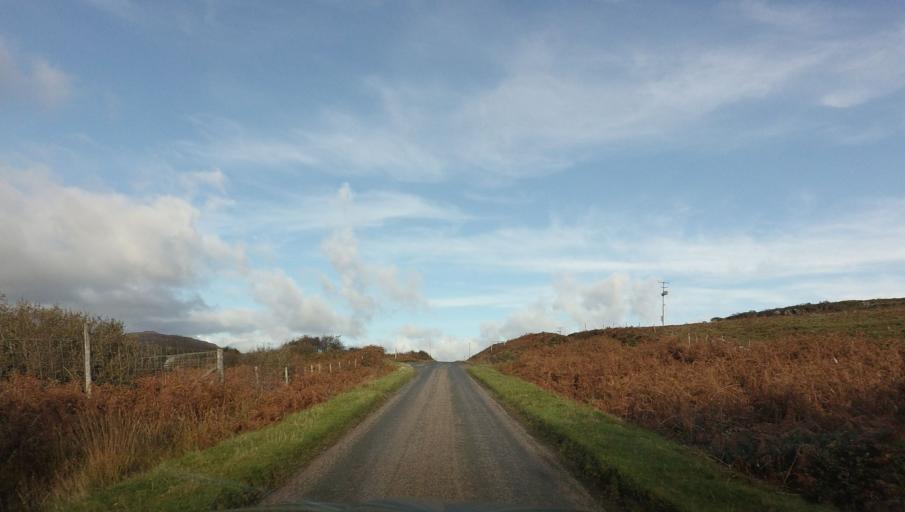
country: GB
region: Scotland
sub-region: Argyll and Bute
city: Isle Of Mull
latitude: 56.3261
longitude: -6.2038
